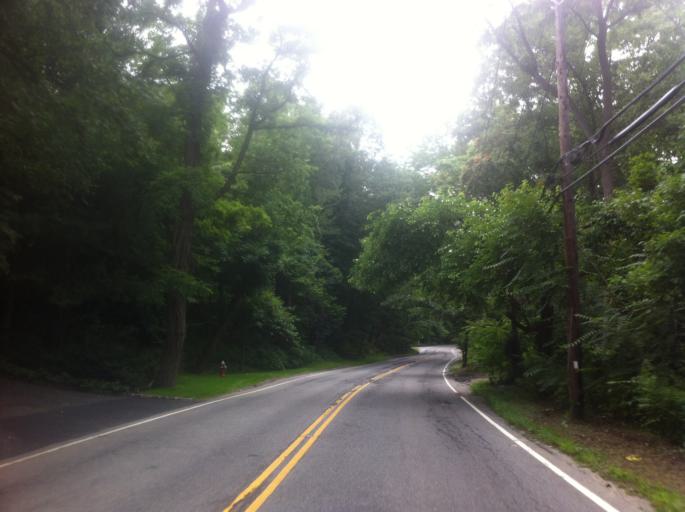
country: US
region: New York
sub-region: Nassau County
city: Oyster Bay
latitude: 40.8681
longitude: -73.5450
